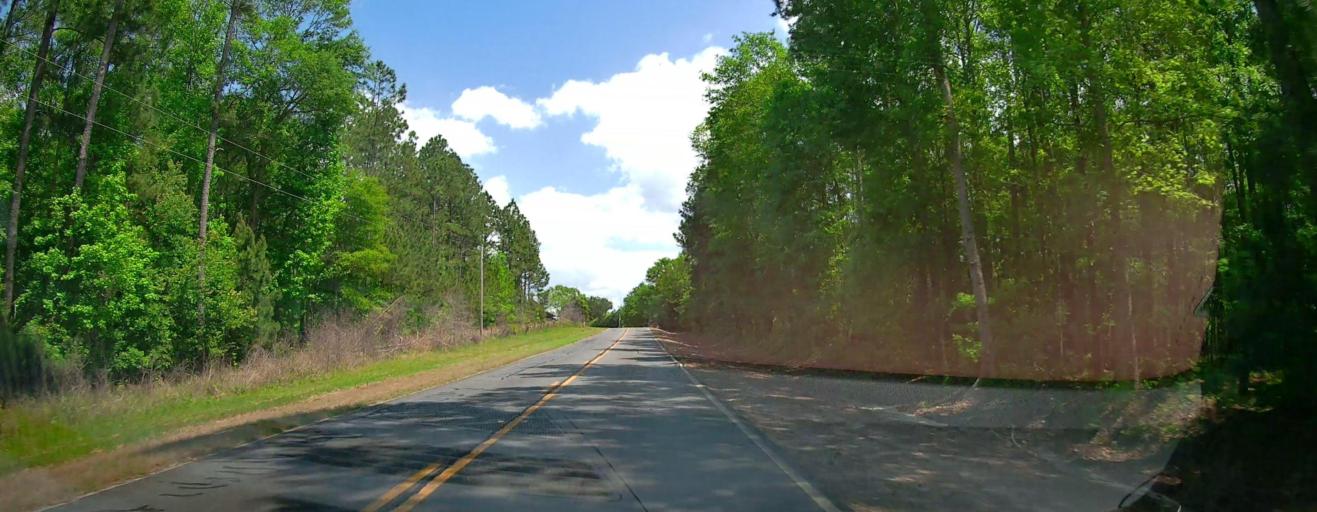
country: US
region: Georgia
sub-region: Treutlen County
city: Soperton
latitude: 32.5079
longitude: -82.6347
